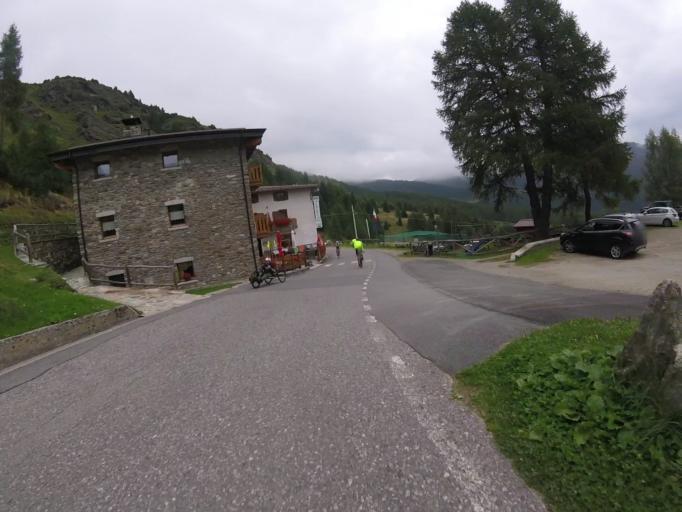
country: IT
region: Lombardy
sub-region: Provincia di Brescia
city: Monno
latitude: 46.2499
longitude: 10.3086
